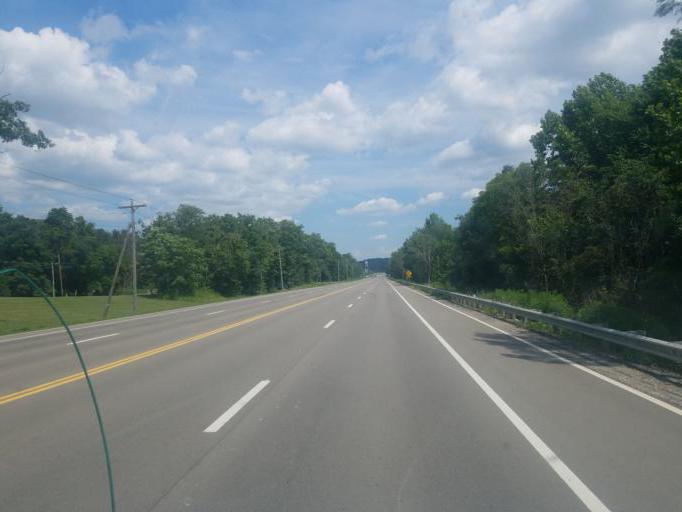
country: US
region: Ohio
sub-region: Muskingum County
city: Zanesville
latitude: 39.9527
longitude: -82.0614
